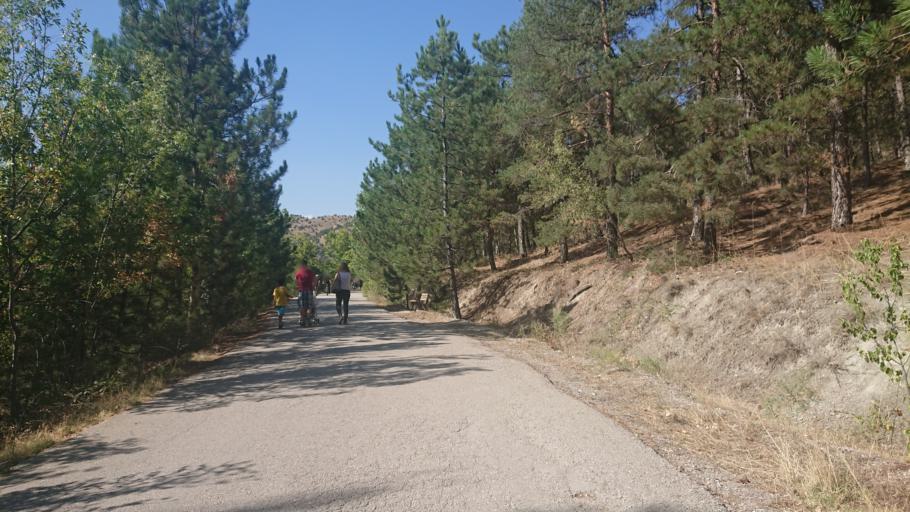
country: TR
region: Ankara
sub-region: Goelbasi
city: Golbasi
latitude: 39.8182
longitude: 32.8211
